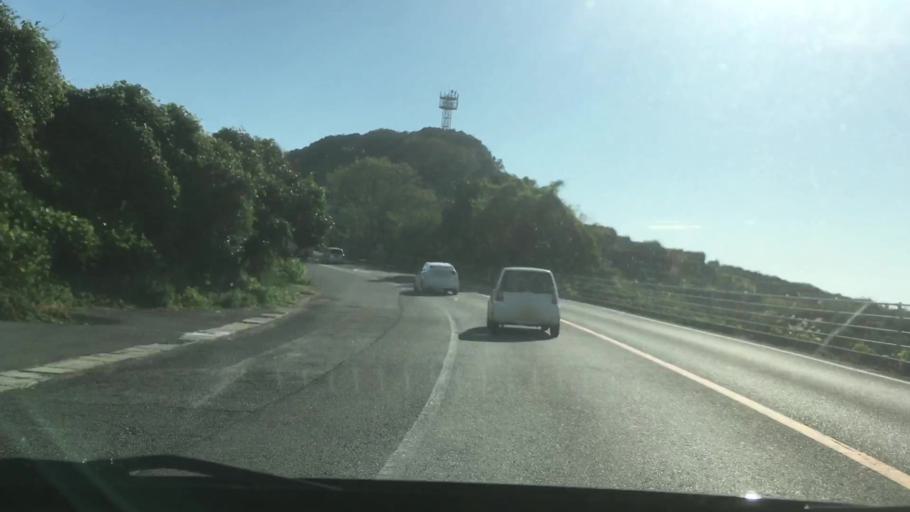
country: JP
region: Nagasaki
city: Sasebo
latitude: 33.0464
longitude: 129.7508
